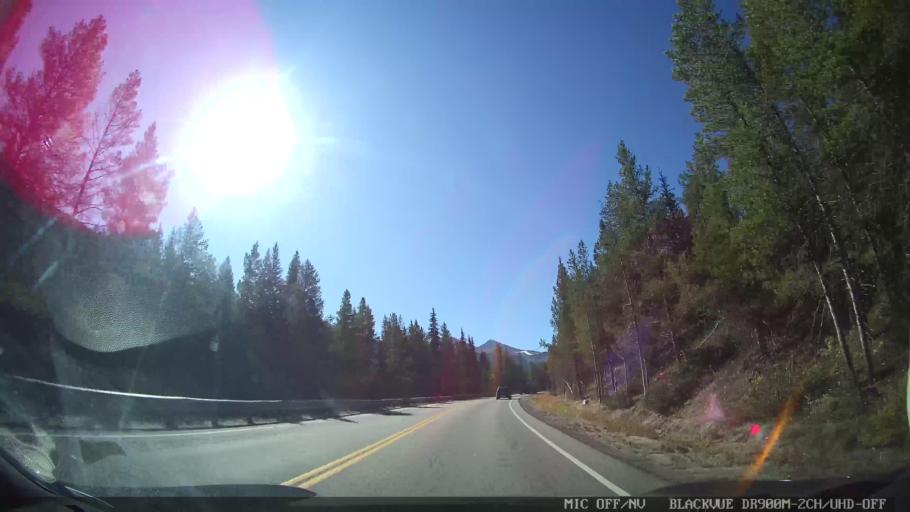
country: US
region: Colorado
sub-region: Summit County
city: Frisco
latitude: 39.4866
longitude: -106.1333
